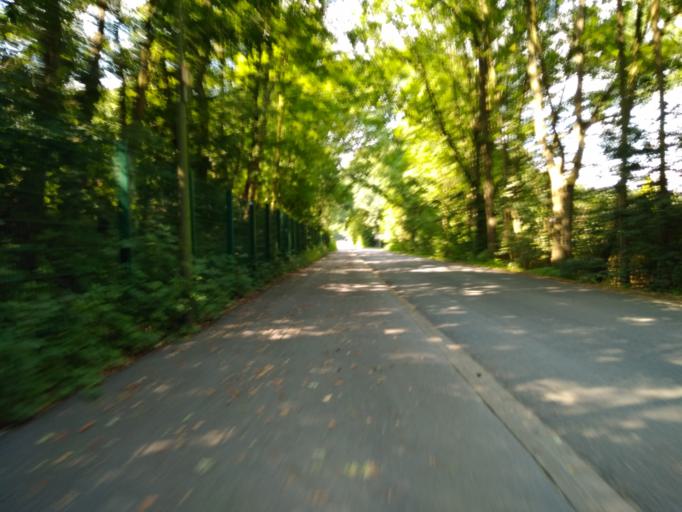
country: DE
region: North Rhine-Westphalia
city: Dorsten
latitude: 51.6839
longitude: 6.9703
